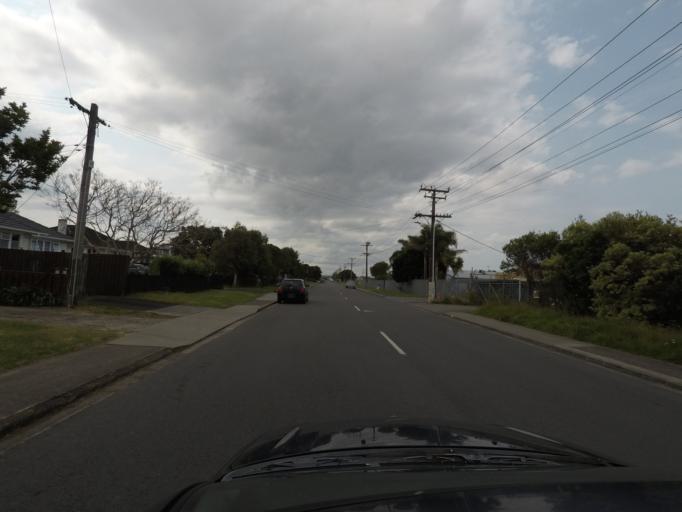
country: NZ
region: Auckland
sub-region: Auckland
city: Rosebank
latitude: -36.8307
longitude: 174.6467
